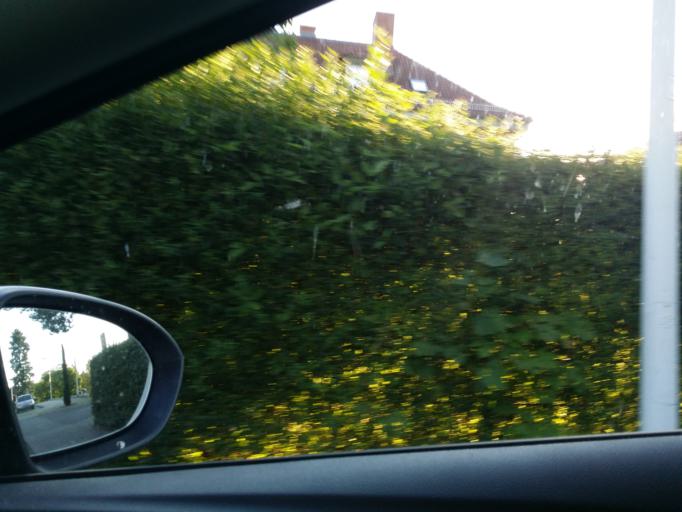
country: DE
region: Hesse
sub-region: Regierungsbezirk Darmstadt
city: Darmstadt
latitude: 49.8387
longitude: 8.6562
